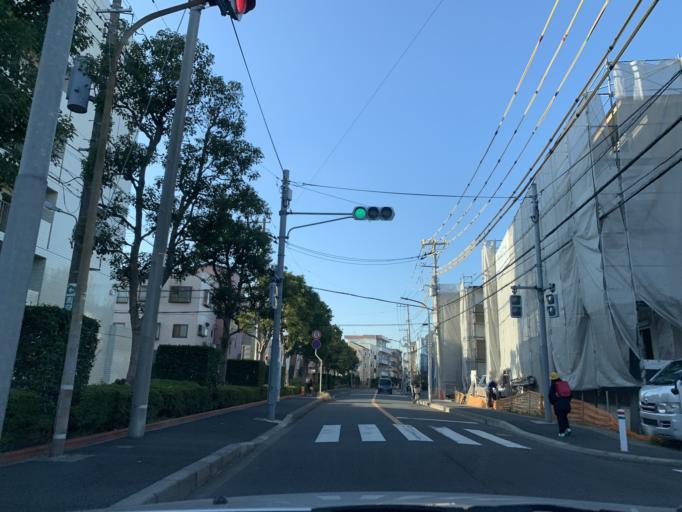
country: JP
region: Tokyo
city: Urayasu
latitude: 35.6685
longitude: 139.9011
